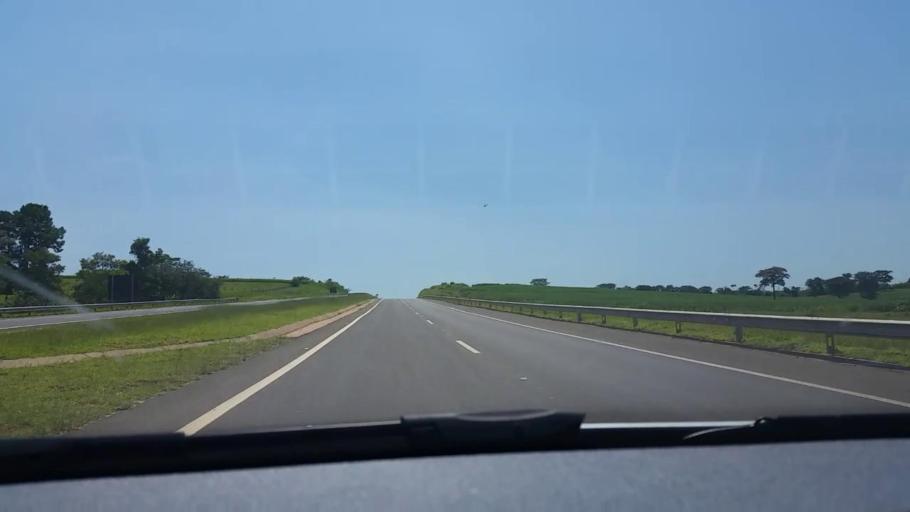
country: BR
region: Sao Paulo
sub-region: Bauru
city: Bauru
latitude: -22.4395
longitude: -49.1440
